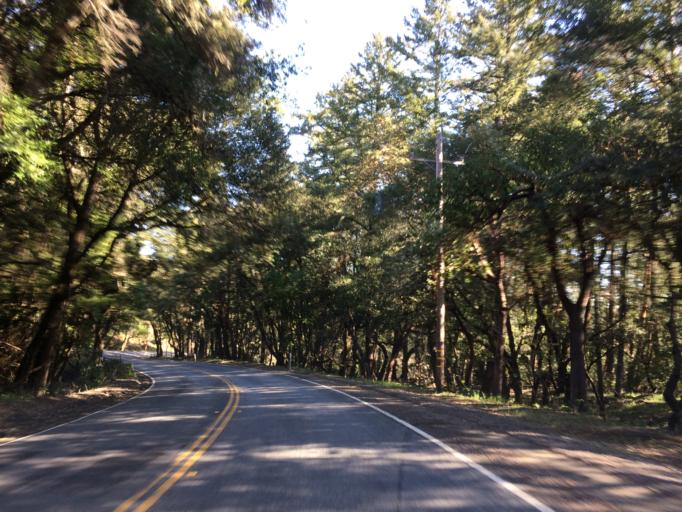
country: US
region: California
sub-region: Santa Clara County
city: Loyola
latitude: 37.2989
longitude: -122.1633
